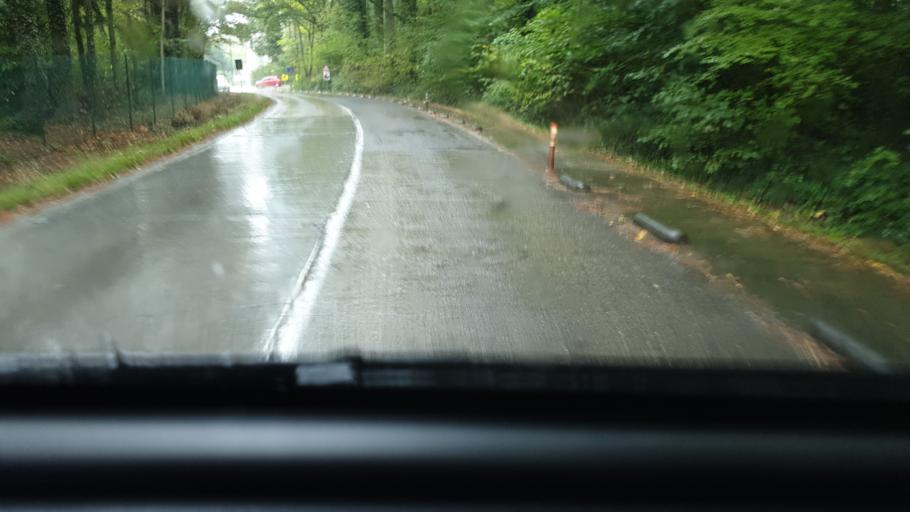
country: BE
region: Wallonia
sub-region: Province du Hainaut
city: Charleroi
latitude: 50.3775
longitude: 4.4821
